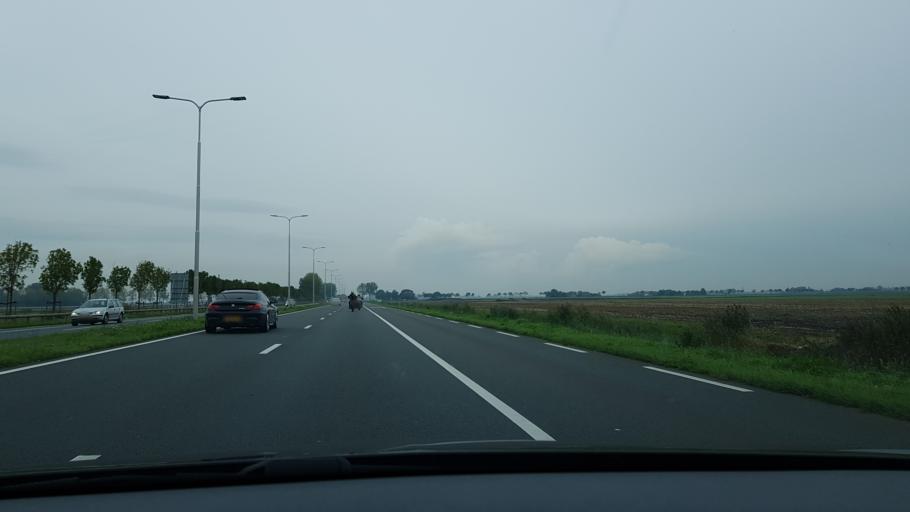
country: NL
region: South Holland
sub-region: Gemeente Alphen aan den Rijn
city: Alphen aan den Rijn
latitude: 52.1594
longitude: 4.6656
